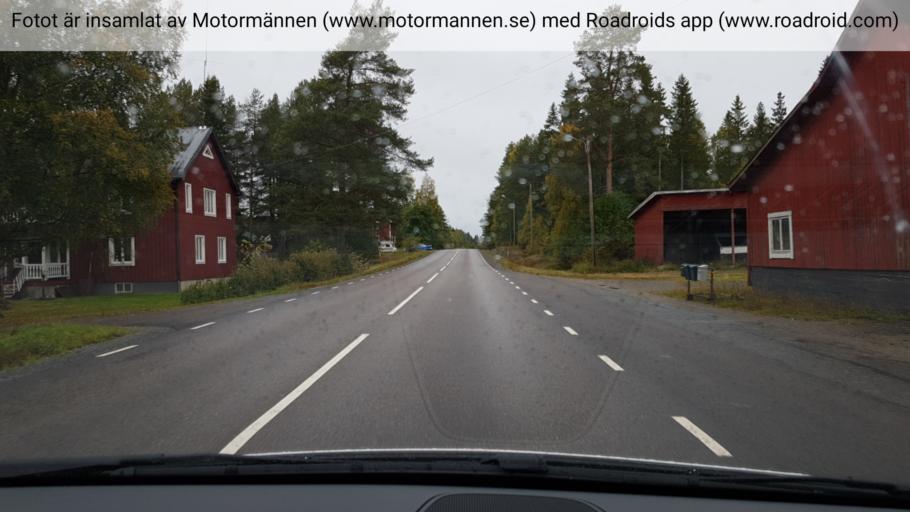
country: SE
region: Vaesterbotten
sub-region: Umea Kommun
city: Ersmark
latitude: 63.9679
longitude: 20.2786
